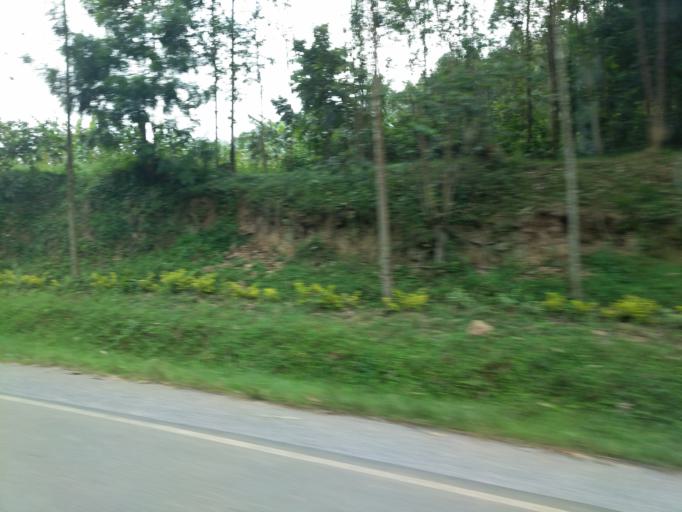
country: RW
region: Northern Province
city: Byumba
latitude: -1.7263
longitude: 29.9199
